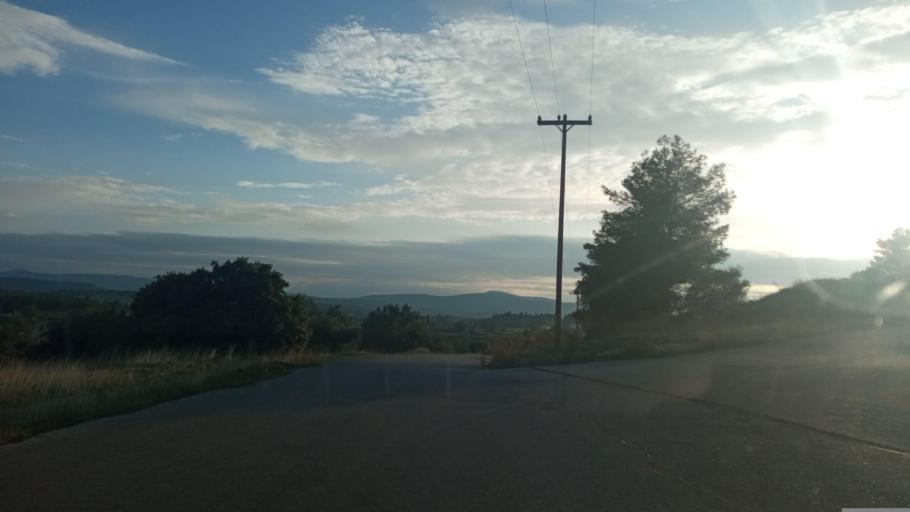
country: GR
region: Central Greece
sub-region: Nomos Evvoias
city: Psachna
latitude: 38.5956
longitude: 23.7231
